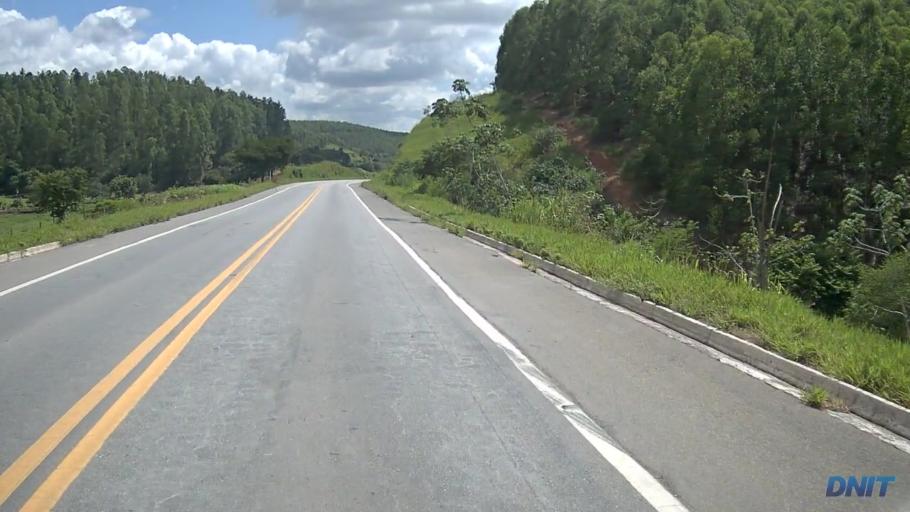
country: BR
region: Minas Gerais
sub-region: Governador Valadares
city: Governador Valadares
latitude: -19.0773
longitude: -42.1802
